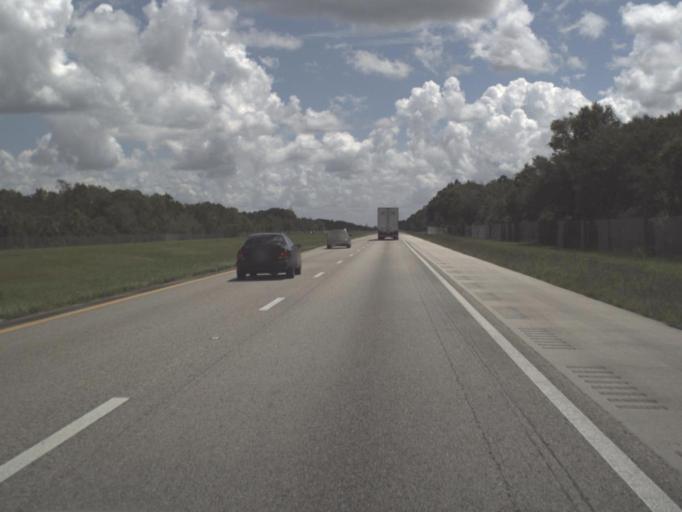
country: US
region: Florida
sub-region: Collier County
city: Orangetree
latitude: 26.1534
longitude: -81.4292
